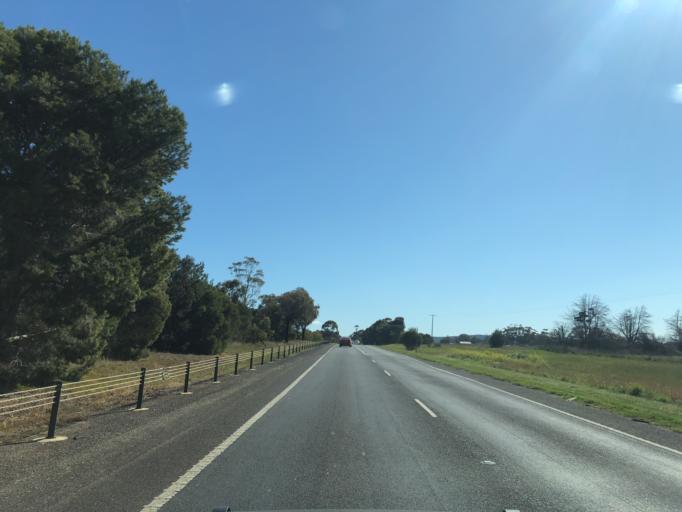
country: AU
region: Victoria
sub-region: Melton
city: Kurunjang
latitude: -37.6266
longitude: 144.6396
